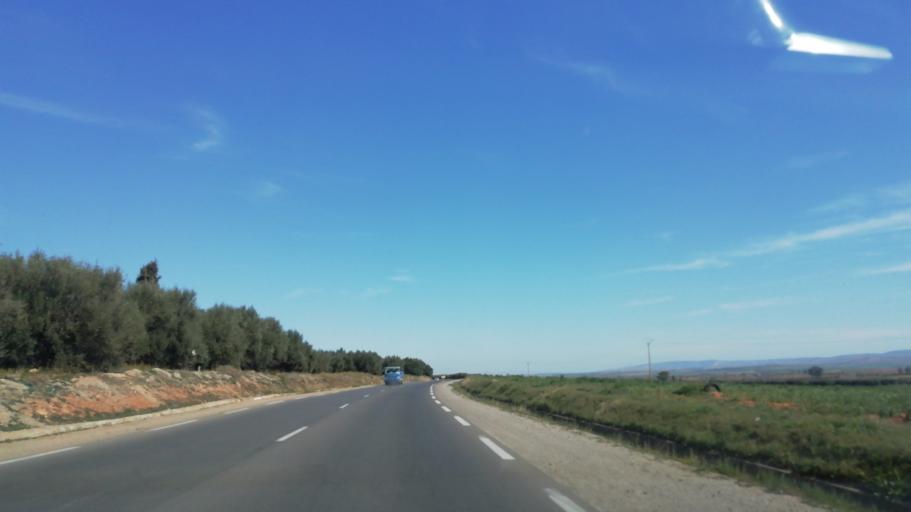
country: DZ
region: Mascara
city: Oued el Abtal
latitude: 35.4194
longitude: 0.4263
